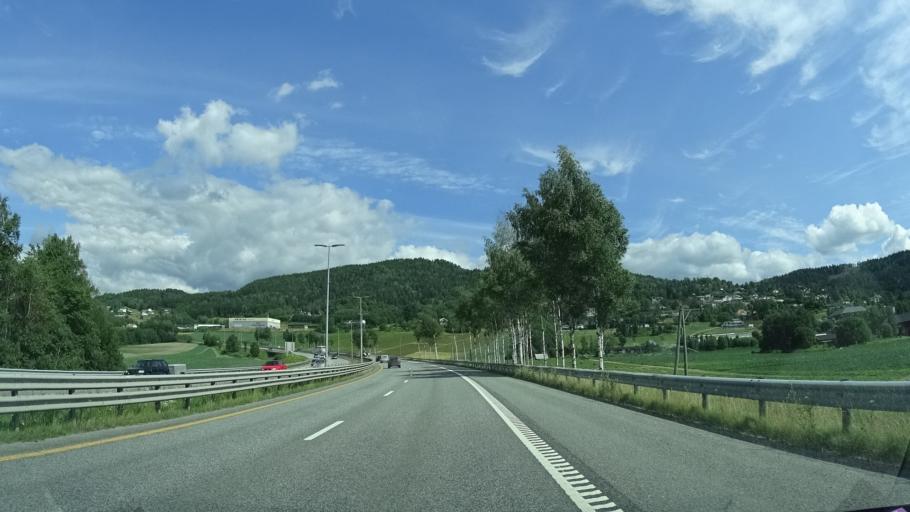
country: NO
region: Buskerud
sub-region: Lier
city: Lierbyen
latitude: 59.7735
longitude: 10.2723
